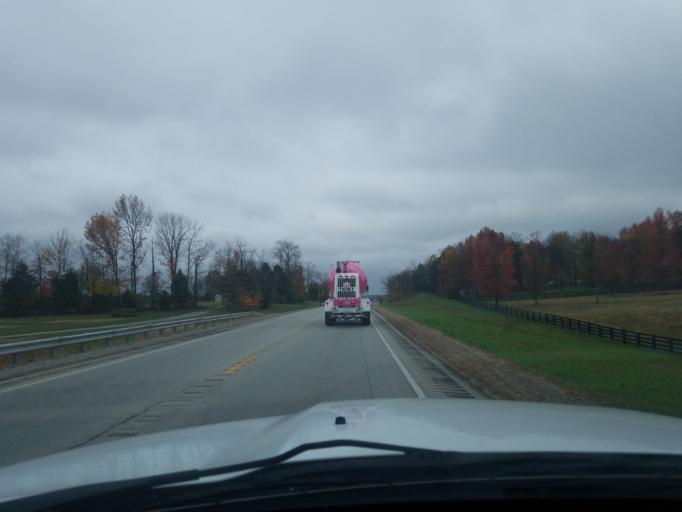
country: US
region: Kentucky
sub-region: Nelson County
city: Bardstown
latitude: 37.8790
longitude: -85.5409
